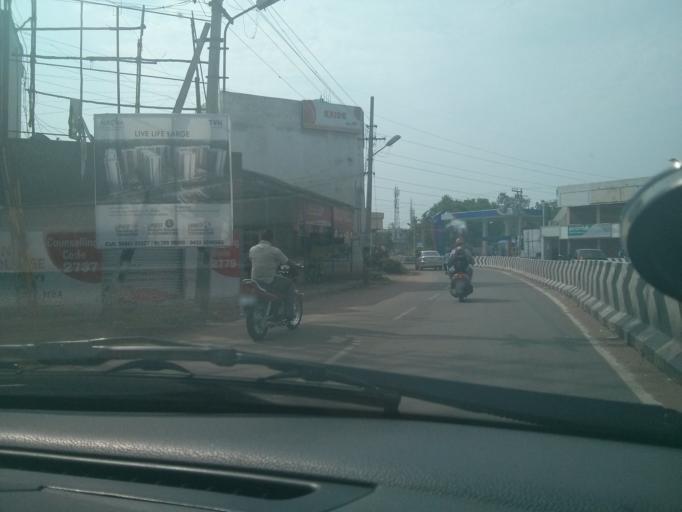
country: IN
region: Tamil Nadu
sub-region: Coimbatore
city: Perur
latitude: 11.0213
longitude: 76.9172
